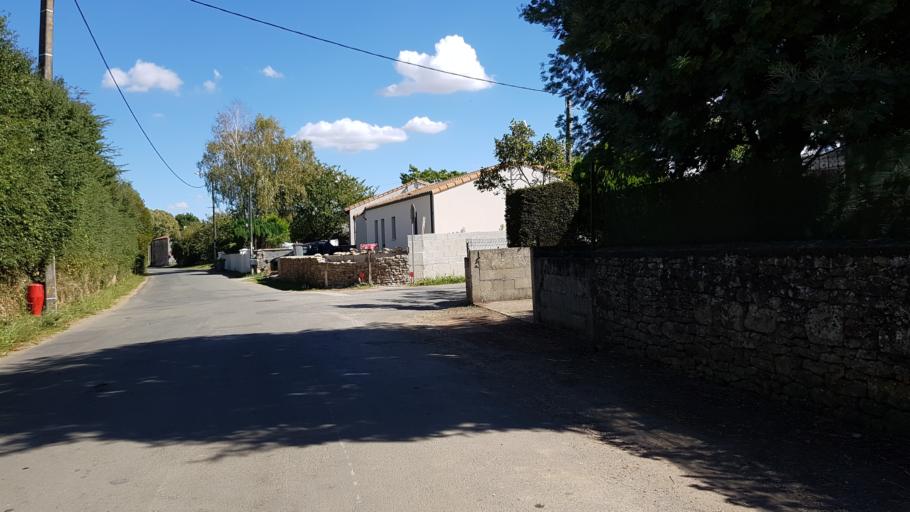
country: FR
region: Poitou-Charentes
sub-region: Departement des Deux-Sevres
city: Vouille
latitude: 46.3089
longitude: -0.3441
